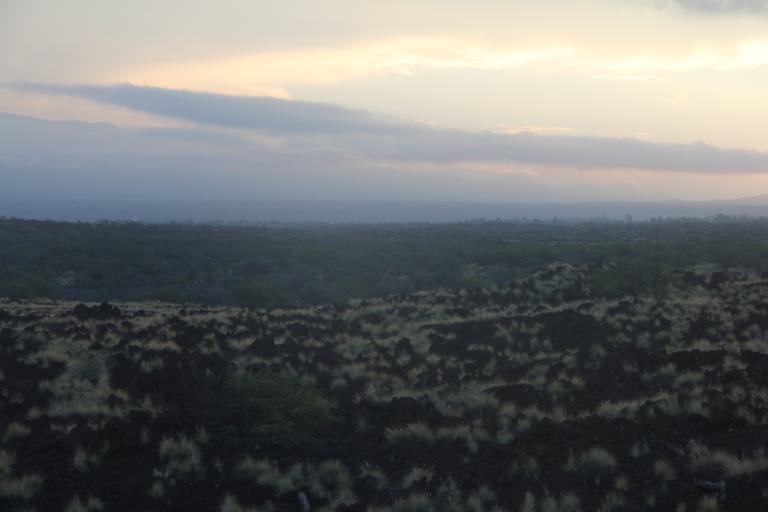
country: US
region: Hawaii
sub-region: Hawaii County
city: Waikoloa Village
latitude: 19.9131
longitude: -155.8222
